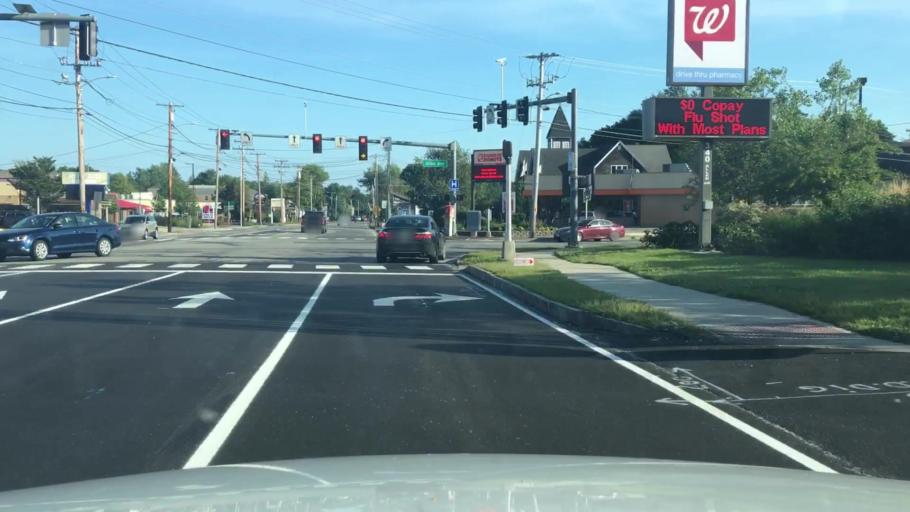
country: US
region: Maine
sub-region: Cumberland County
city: Portland
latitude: 43.7000
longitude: -70.2885
